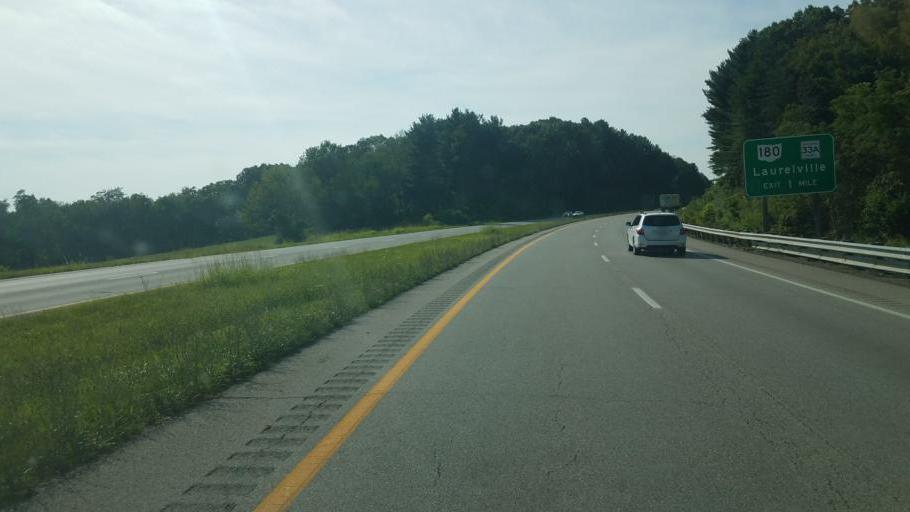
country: US
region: Ohio
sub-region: Hocking County
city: Logan
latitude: 39.5513
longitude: -82.4734
